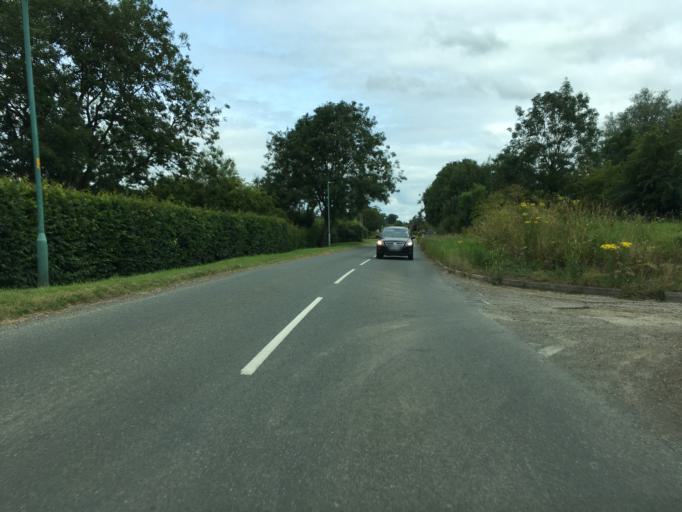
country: GB
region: England
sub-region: Gloucestershire
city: Bourton on the Water
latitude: 51.8756
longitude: -1.7402
